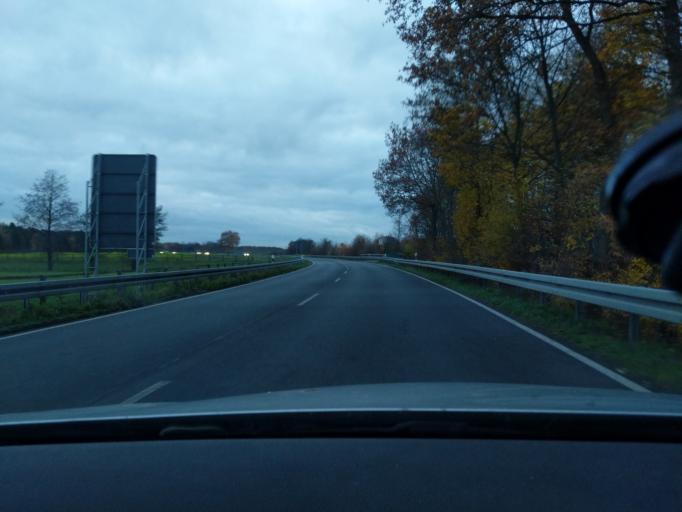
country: DE
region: North Rhine-Westphalia
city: Olfen
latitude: 51.7089
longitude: 7.4242
